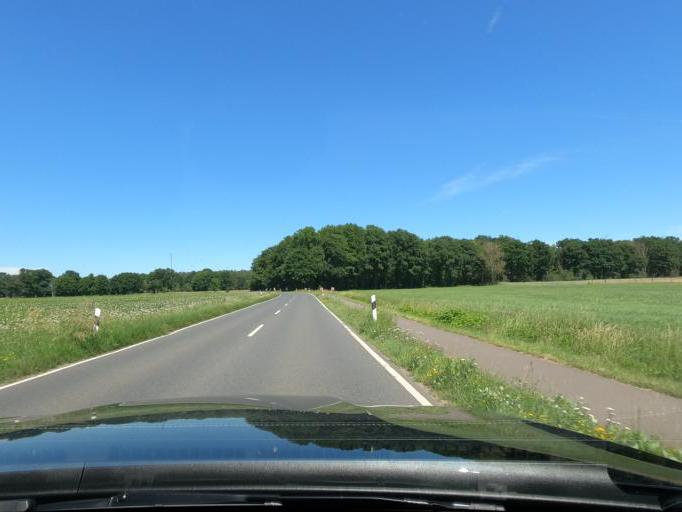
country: DE
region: Lower Saxony
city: Eicklingen
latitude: 52.5629
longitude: 10.1873
